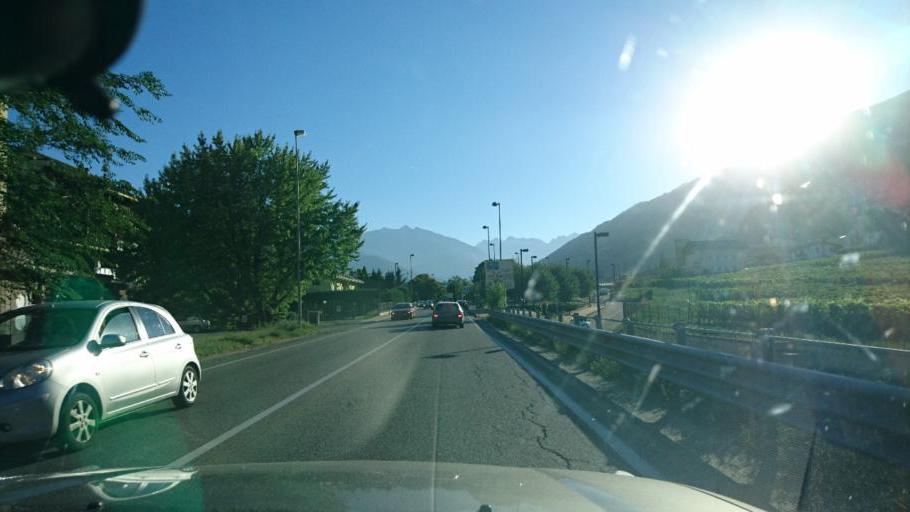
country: IT
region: Aosta Valley
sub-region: Valle d'Aosta
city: Aosta
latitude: 45.7373
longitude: 7.3029
